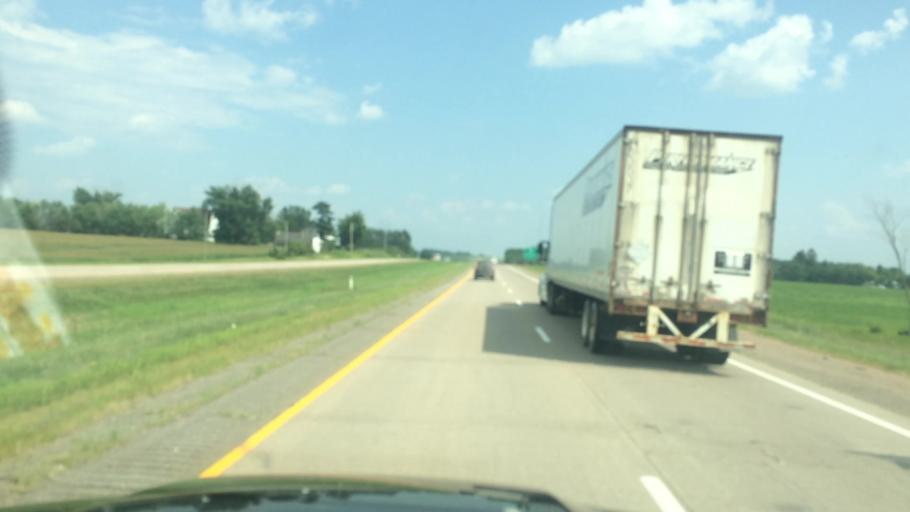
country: US
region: Wisconsin
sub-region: Marathon County
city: Athens
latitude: 44.9454
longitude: -90.1096
